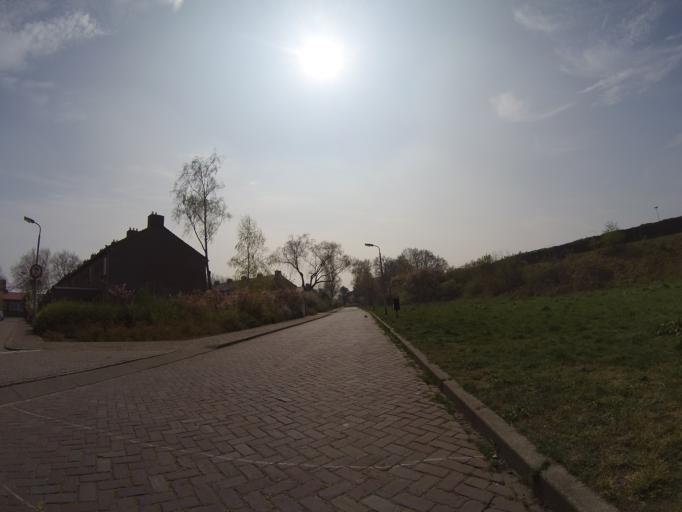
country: NL
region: Utrecht
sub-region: Gemeente Amersfoort
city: Hoogland
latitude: 52.1607
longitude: 5.3499
